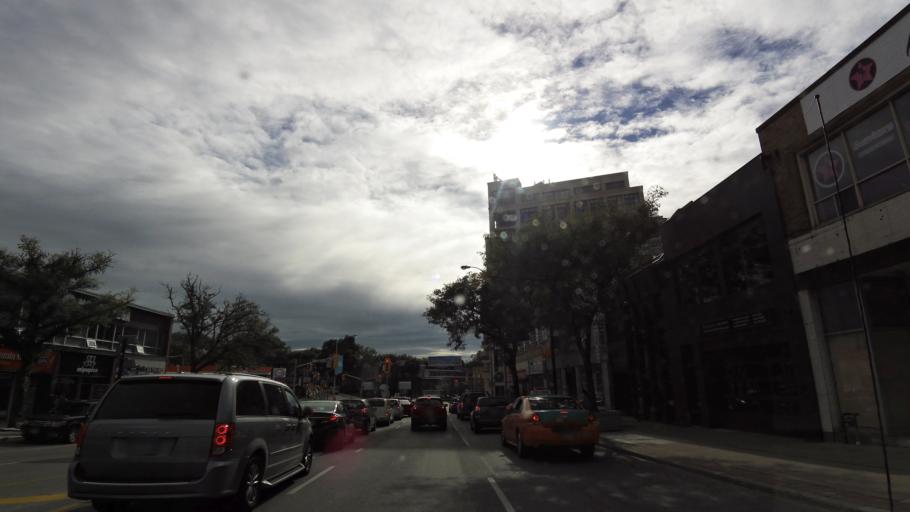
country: CA
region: Ontario
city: Etobicoke
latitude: 43.6490
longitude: -79.4850
